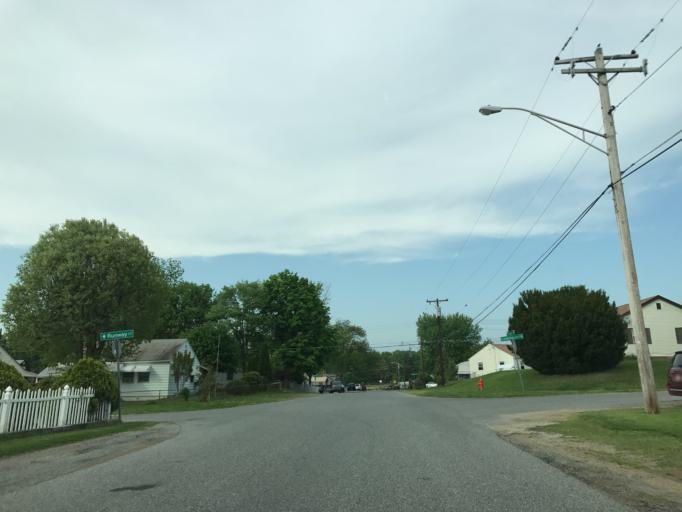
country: US
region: Maryland
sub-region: Baltimore County
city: Middle River
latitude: 39.3393
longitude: -76.4588
